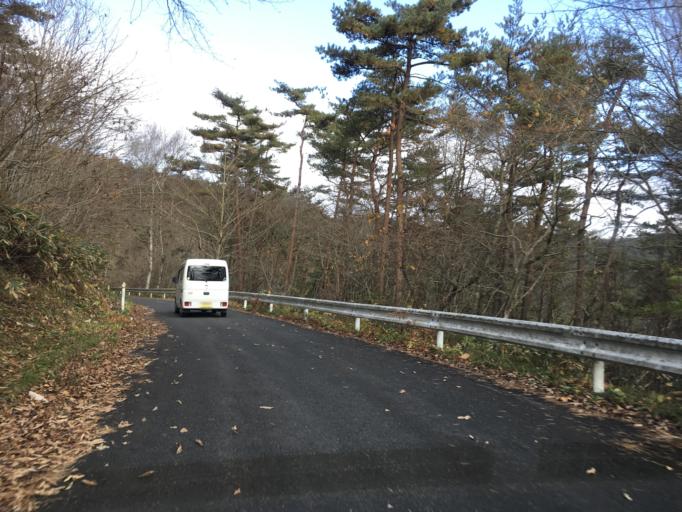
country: JP
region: Iwate
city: Mizusawa
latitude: 39.1237
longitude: 141.3051
